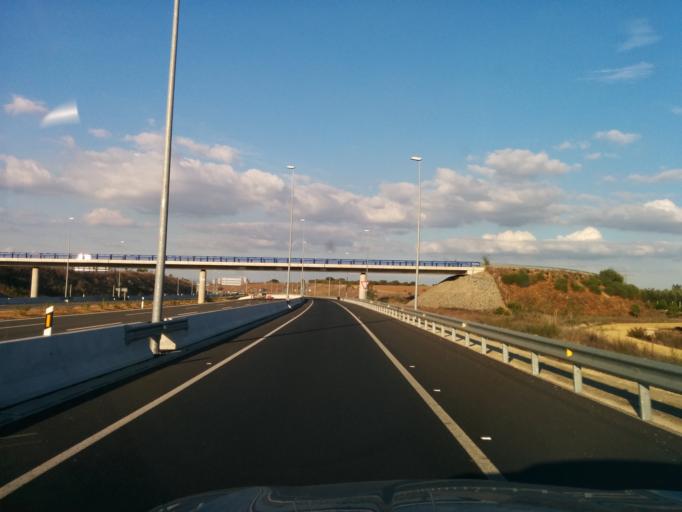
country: ES
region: Andalusia
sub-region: Provincia de Sevilla
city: Dos Hermanas
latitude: 37.3209
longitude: -5.8937
